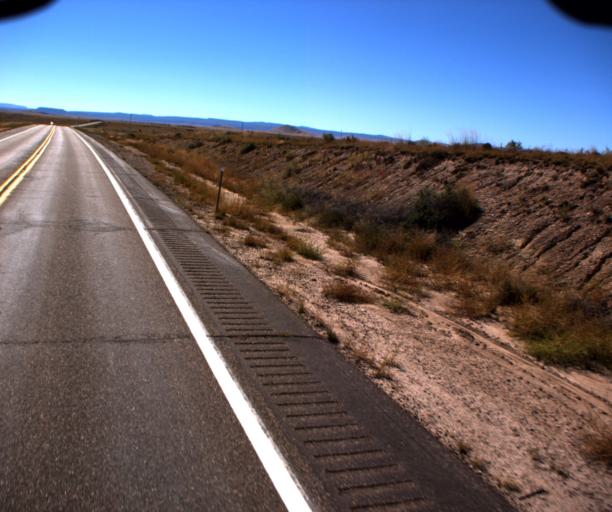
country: US
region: Arizona
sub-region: Apache County
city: Saint Johns
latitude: 34.3268
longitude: -109.3861
